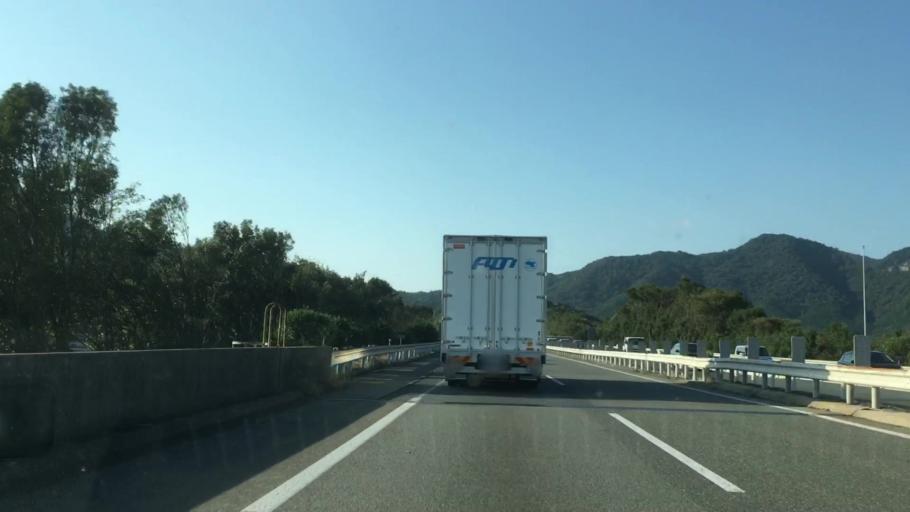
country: JP
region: Yamaguchi
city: Hofu
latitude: 34.0714
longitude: 131.4971
